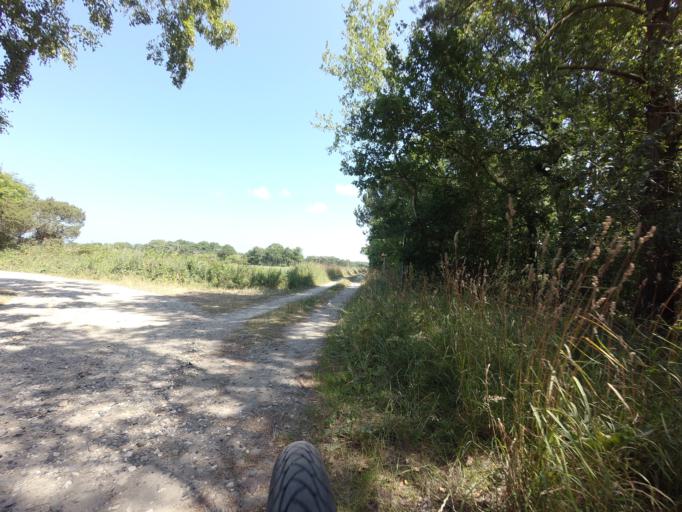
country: DK
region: North Denmark
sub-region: Laeso Kommune
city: Byrum
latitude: 57.2526
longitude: 10.9042
